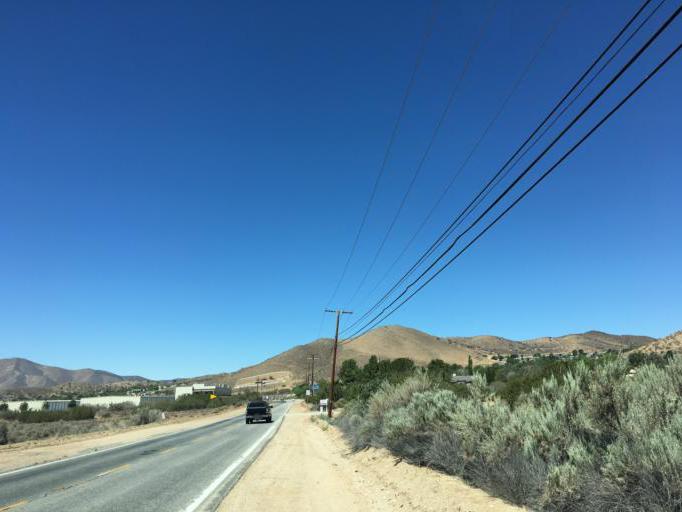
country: US
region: California
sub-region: Los Angeles County
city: Acton
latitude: 34.4810
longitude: -118.1597
